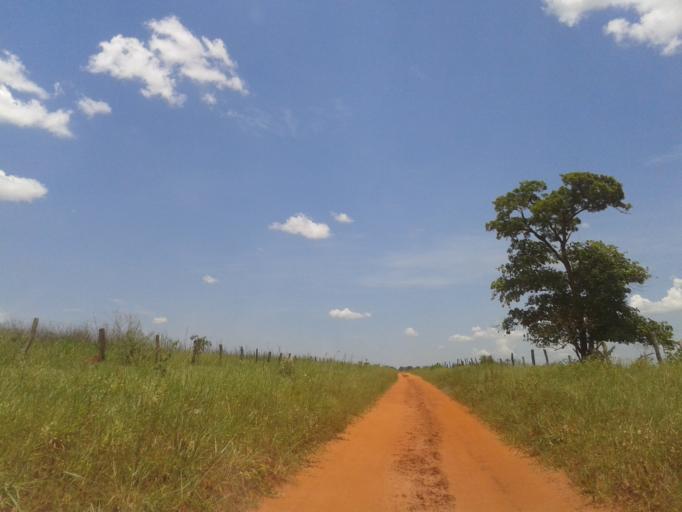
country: BR
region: Minas Gerais
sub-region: Santa Vitoria
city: Santa Vitoria
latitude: -19.2223
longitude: -50.4377
